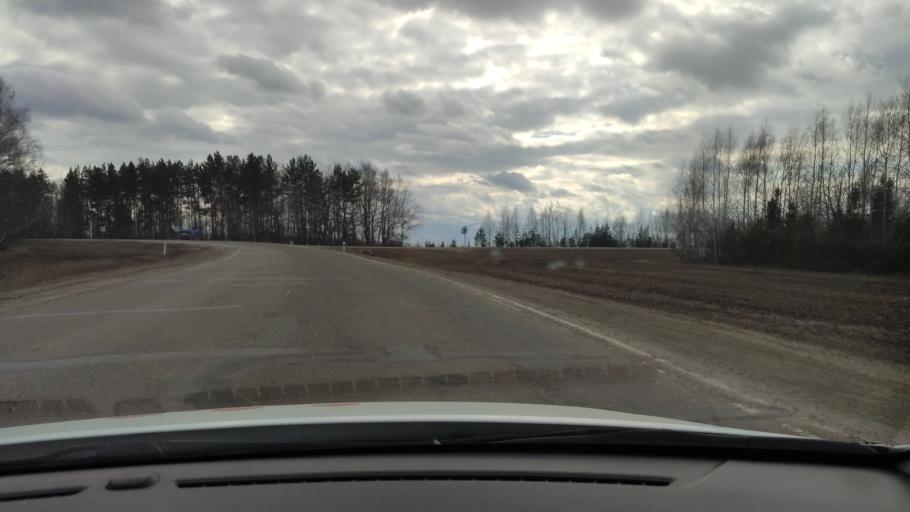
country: RU
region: Tatarstan
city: Vysokaya Gora
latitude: 56.1050
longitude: 49.1790
